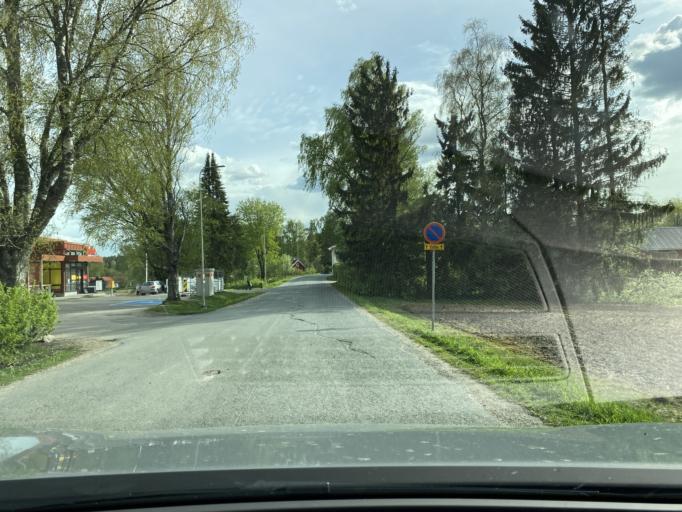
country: FI
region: Varsinais-Suomi
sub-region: Salo
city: Kiikala
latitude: 60.4605
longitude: 23.5514
